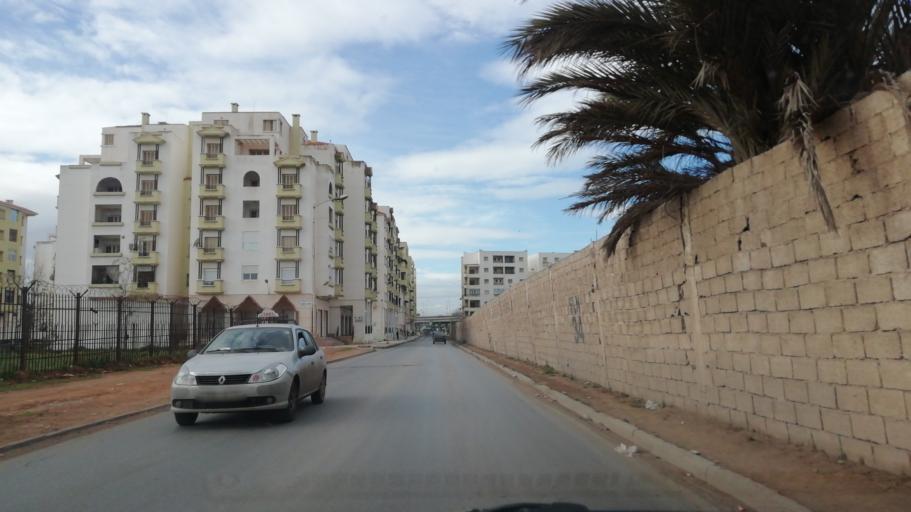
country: DZ
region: Oran
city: Oran
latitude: 35.6851
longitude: -0.6065
